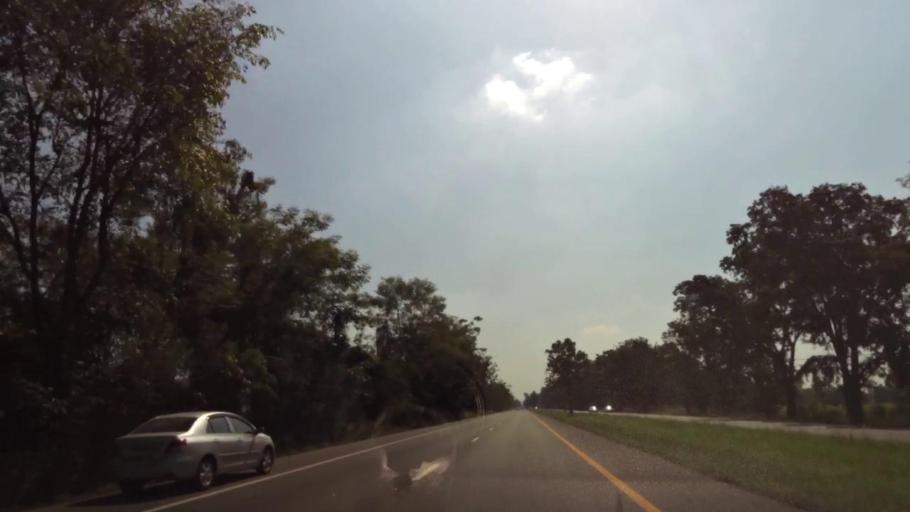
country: TH
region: Phichit
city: Bueng Na Rang
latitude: 16.2111
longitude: 100.1272
